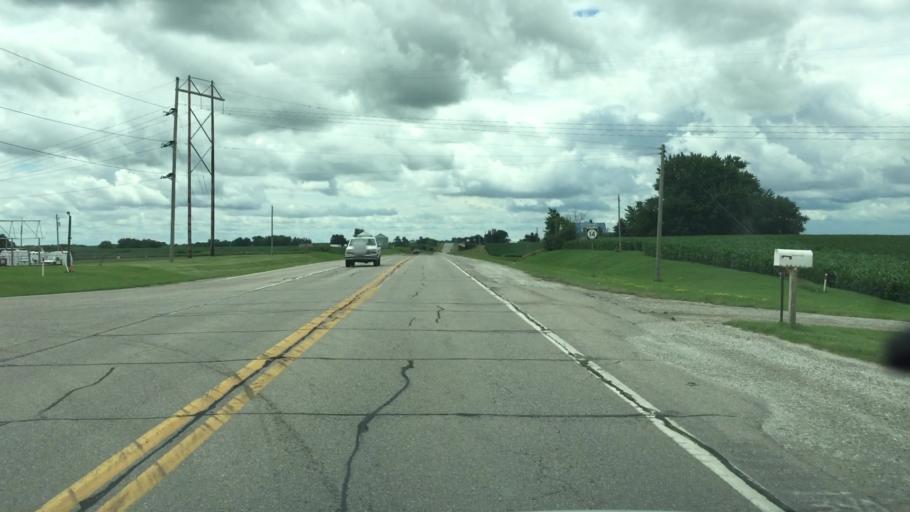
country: US
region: Iowa
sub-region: Jasper County
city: Monroe
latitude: 41.5737
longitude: -93.0970
